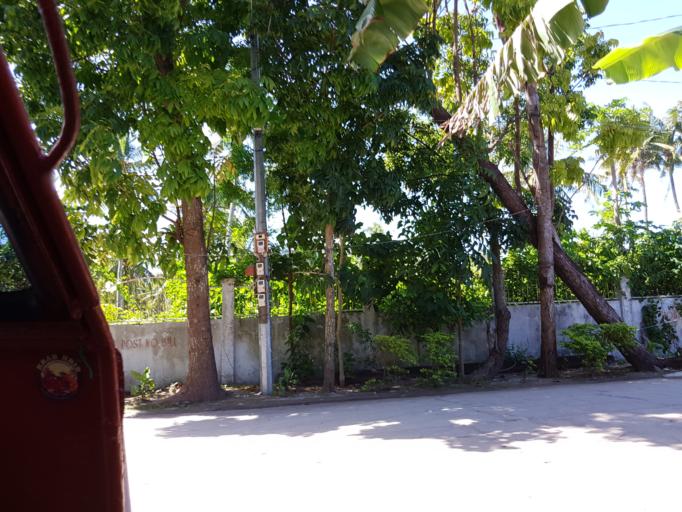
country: PH
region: Central Visayas
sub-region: Province of Cebu
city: Santa Fe
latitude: 11.1525
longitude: 123.8032
